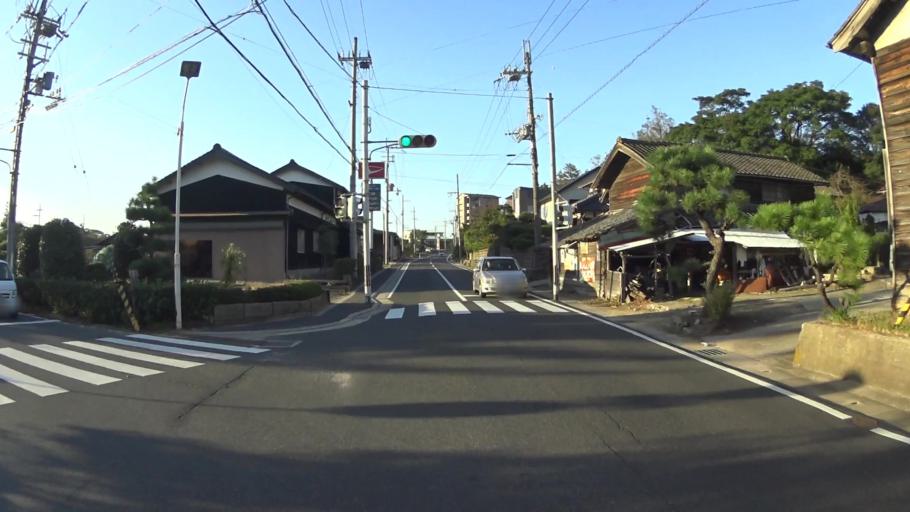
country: JP
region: Hyogo
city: Toyooka
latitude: 35.6565
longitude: 134.9682
